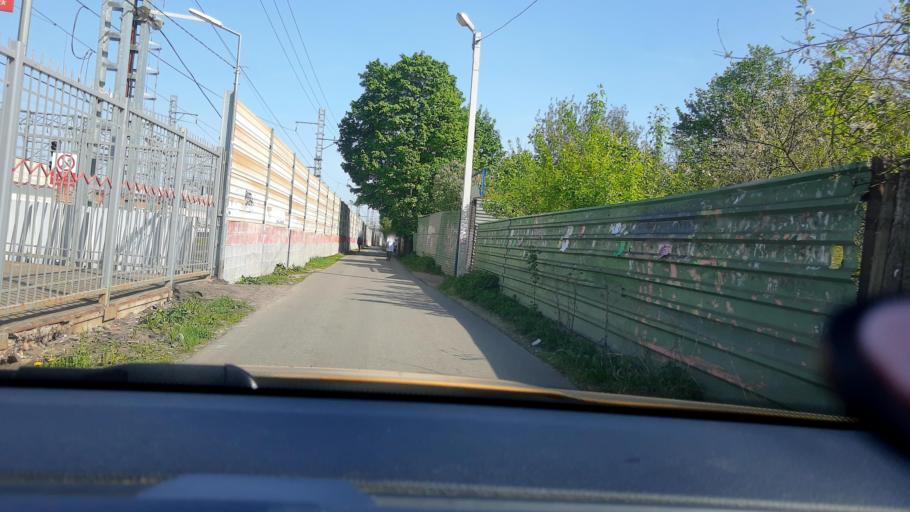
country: RU
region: Moskovskaya
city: Skhodnya
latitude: 55.9488
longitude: 37.3022
